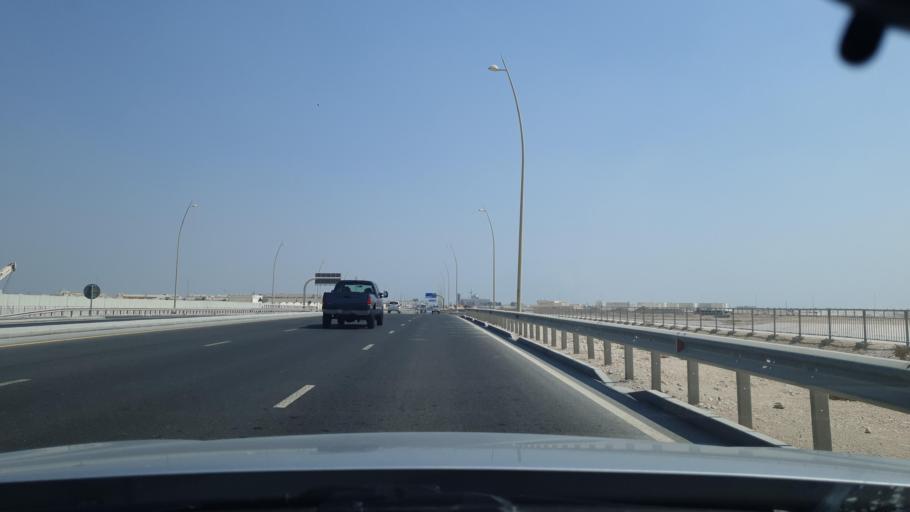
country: QA
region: Al Khawr
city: Al Khawr
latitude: 25.6606
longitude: 51.4856
